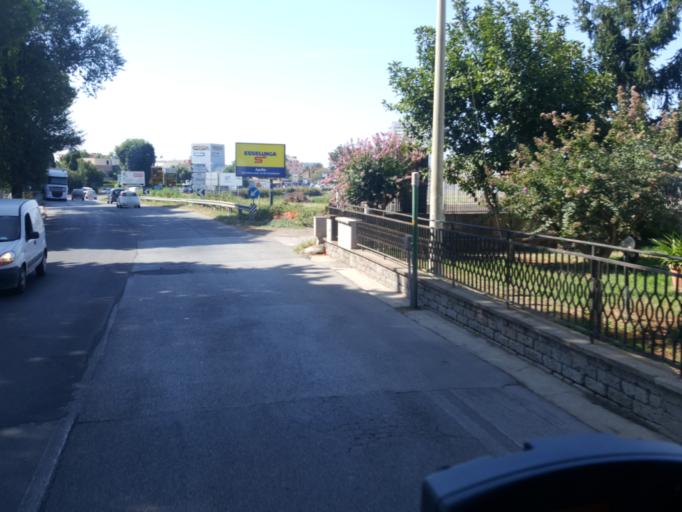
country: IT
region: Latium
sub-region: Citta metropolitana di Roma Capitale
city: Area Produttiva
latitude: 41.6852
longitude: 12.5119
